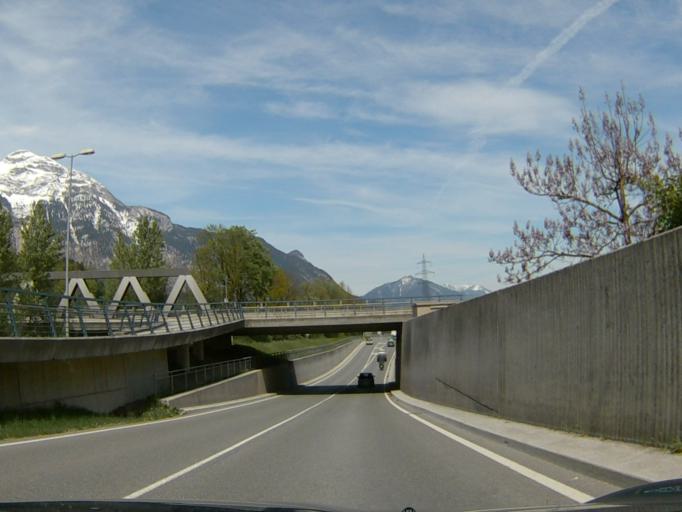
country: AT
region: Tyrol
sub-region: Politischer Bezirk Schwaz
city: Wiesing
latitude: 47.3914
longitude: 11.7964
